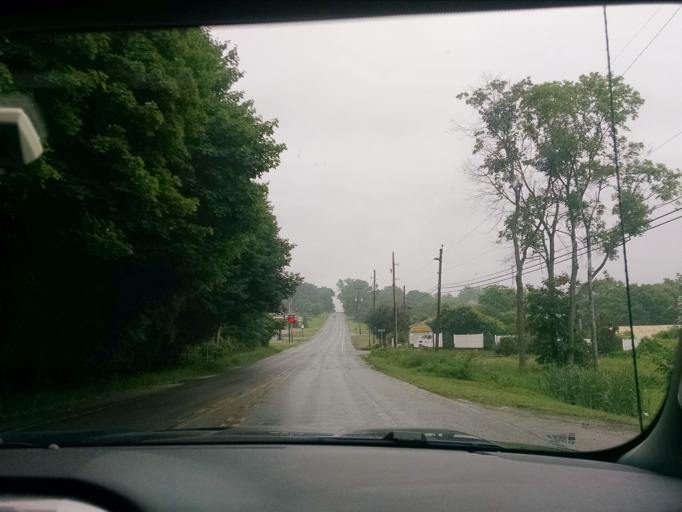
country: US
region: Pennsylvania
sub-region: Indiana County
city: Chevy Chase Heights
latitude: 40.6383
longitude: -79.1391
